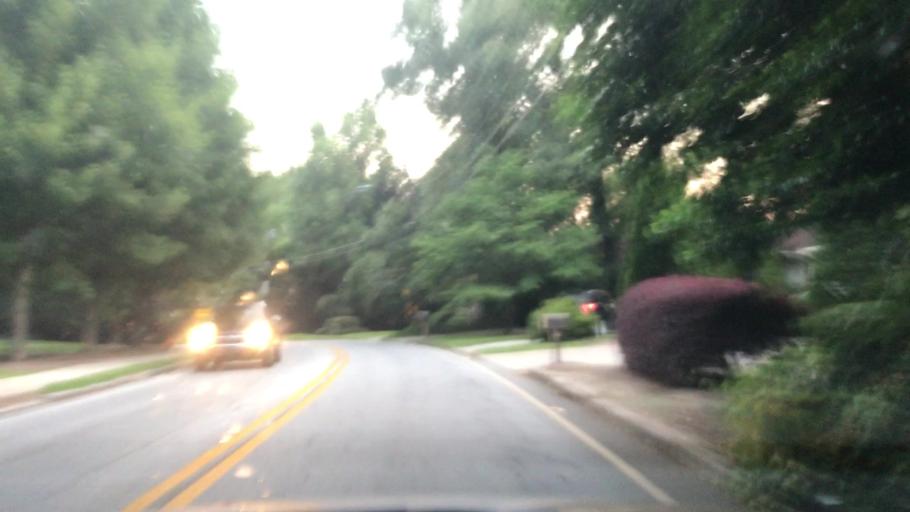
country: US
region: Georgia
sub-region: DeKalb County
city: Druid Hills
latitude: 33.7924
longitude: -84.3390
